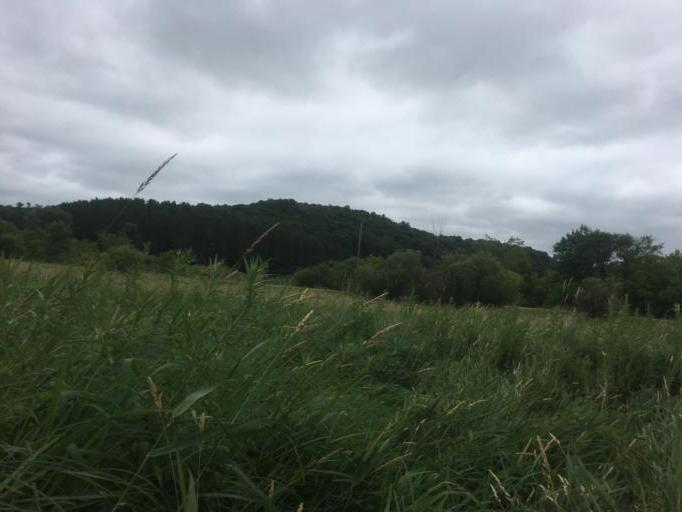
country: US
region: Wisconsin
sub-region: Dunn County
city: Boyceville
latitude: 44.9775
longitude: -92.1069
